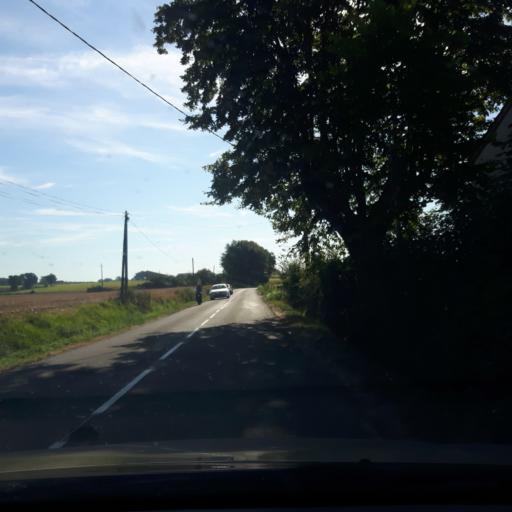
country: FR
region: Midi-Pyrenees
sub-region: Departement de la Haute-Garonne
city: Villeneuve-les-Bouloc
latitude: 43.7621
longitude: 1.4181
